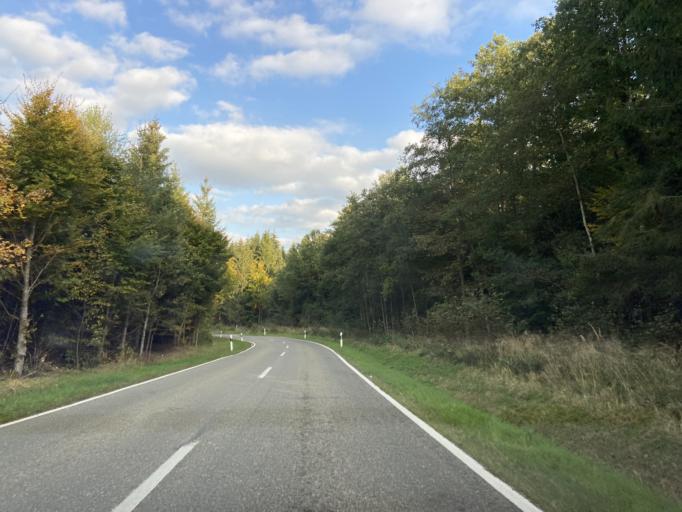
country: DE
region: Baden-Wuerttemberg
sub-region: Tuebingen Region
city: Scheer
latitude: 48.0832
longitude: 9.3095
